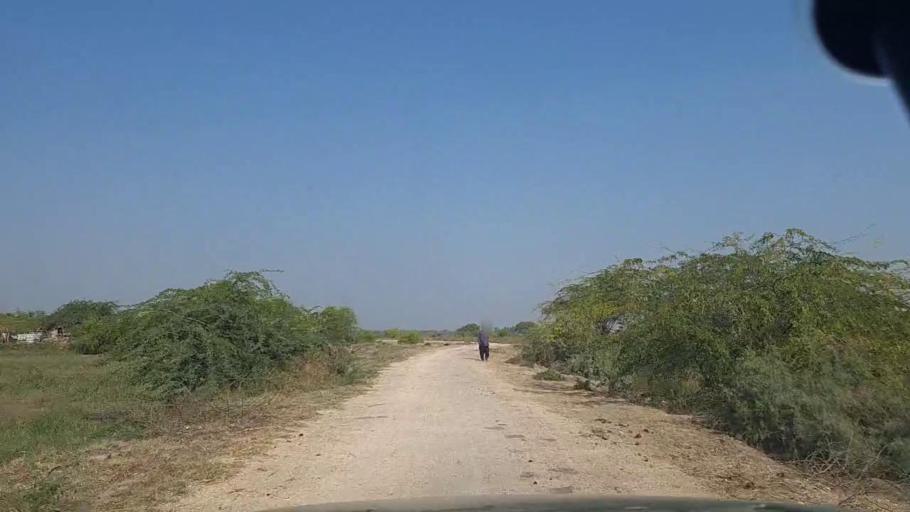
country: PK
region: Sindh
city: Chuhar Jamali
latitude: 24.5191
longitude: 67.8911
